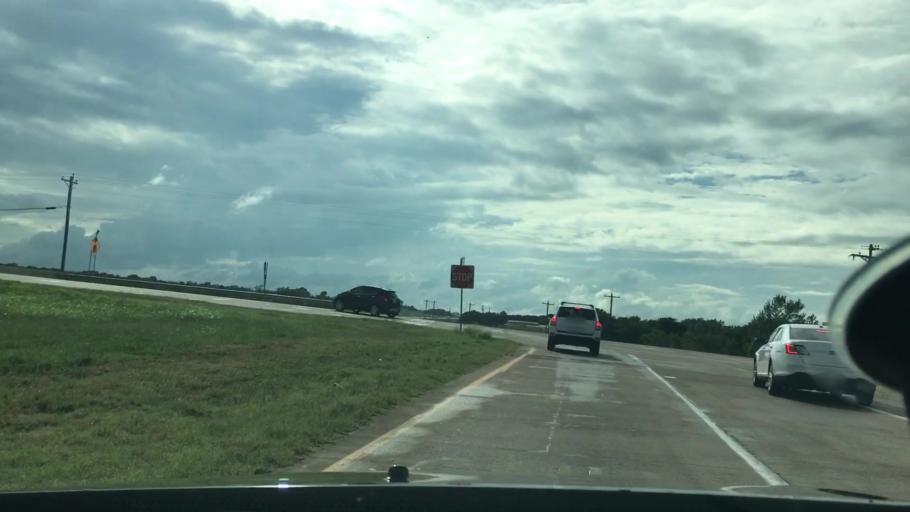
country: US
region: Oklahoma
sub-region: Lincoln County
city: Prague
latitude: 35.3844
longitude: -96.6708
